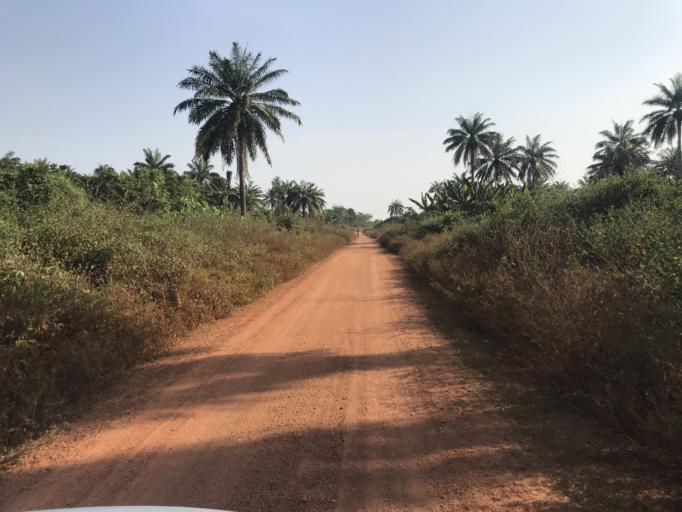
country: NG
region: Osun
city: Bode Osi
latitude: 7.7772
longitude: 4.3034
